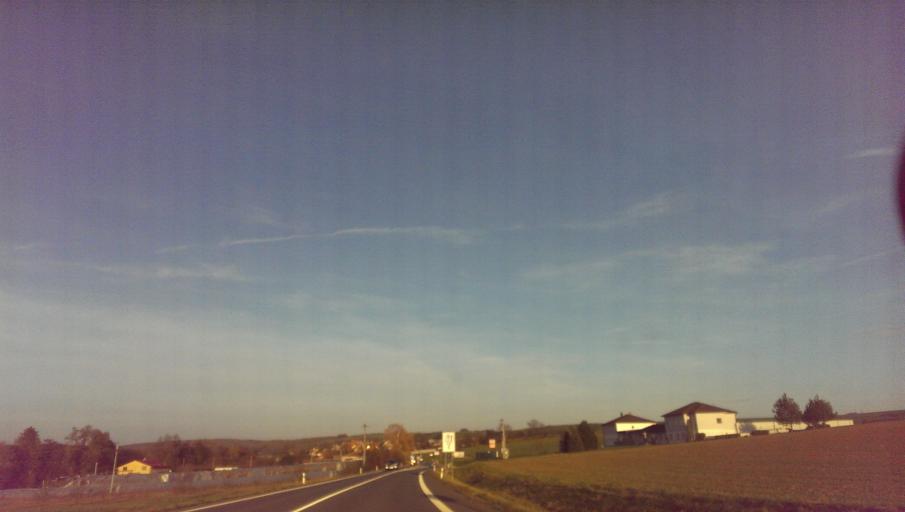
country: CZ
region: Zlin
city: Brezolupy
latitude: 49.1134
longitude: 17.5683
